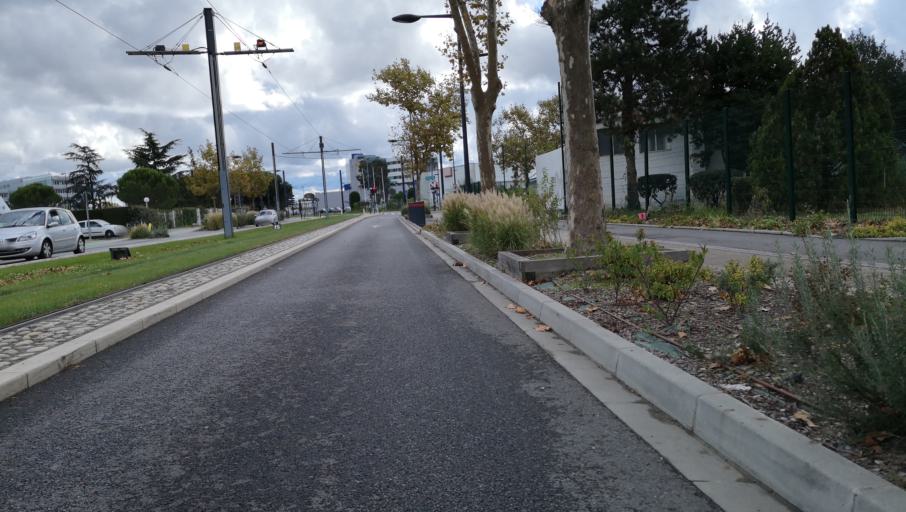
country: FR
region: Midi-Pyrenees
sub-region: Departement de la Haute-Garonne
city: Blagnac
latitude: 43.6265
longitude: 1.3813
